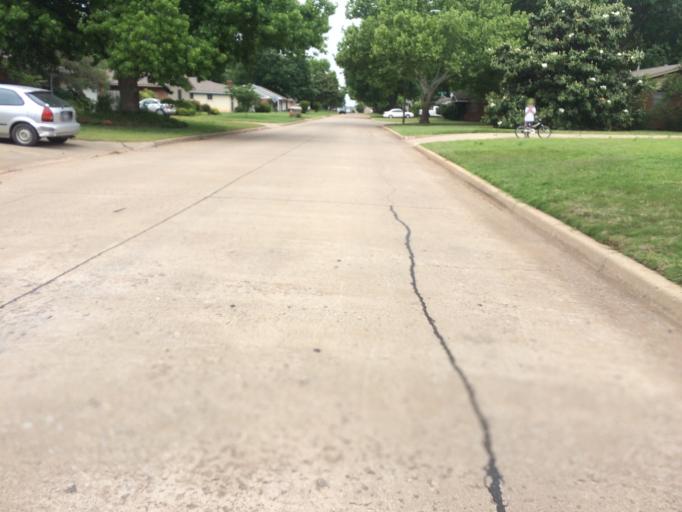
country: US
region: Oklahoma
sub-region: Cleveland County
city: Norman
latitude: 35.2143
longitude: -97.4798
